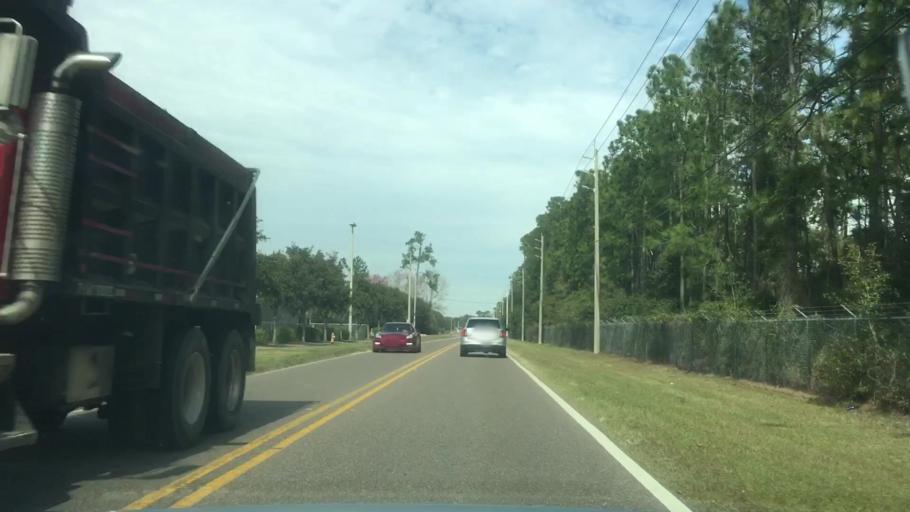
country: US
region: Florida
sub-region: Duval County
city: Jacksonville
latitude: 30.4461
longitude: -81.5581
